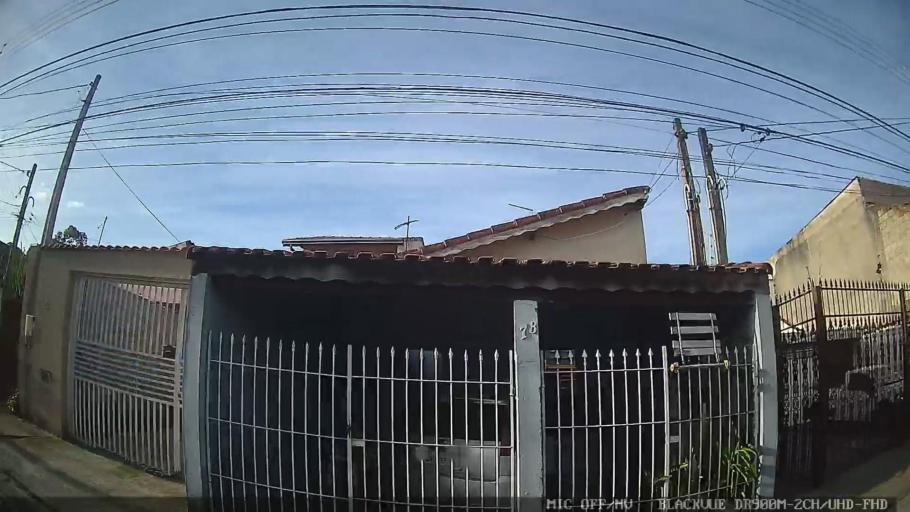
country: BR
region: Sao Paulo
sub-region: Mogi das Cruzes
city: Mogi das Cruzes
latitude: -23.5189
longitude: -46.1429
